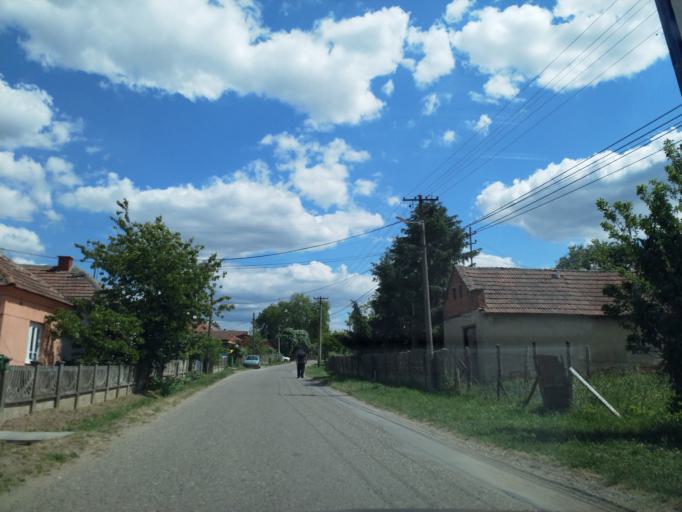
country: RS
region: Central Serbia
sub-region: Pomoravski Okrug
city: Jagodina
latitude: 43.9435
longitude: 21.2979
